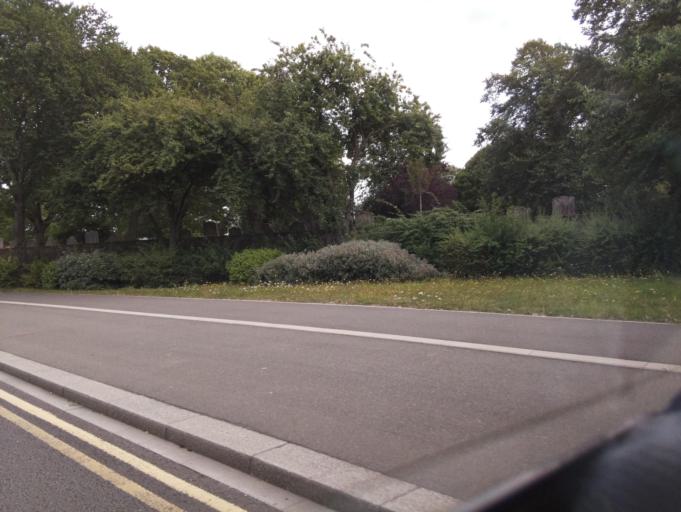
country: GB
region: England
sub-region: Poole
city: Poole
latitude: 50.7169
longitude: -1.9859
